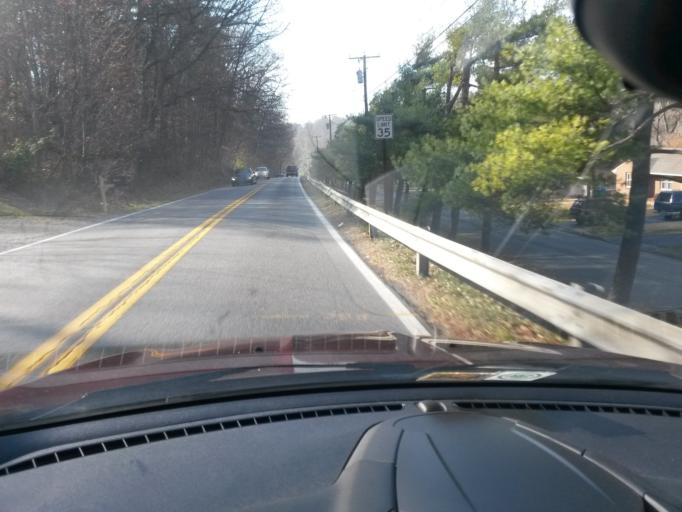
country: US
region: Virginia
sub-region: Roanoke County
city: Cave Spring
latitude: 37.2431
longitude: -79.9785
